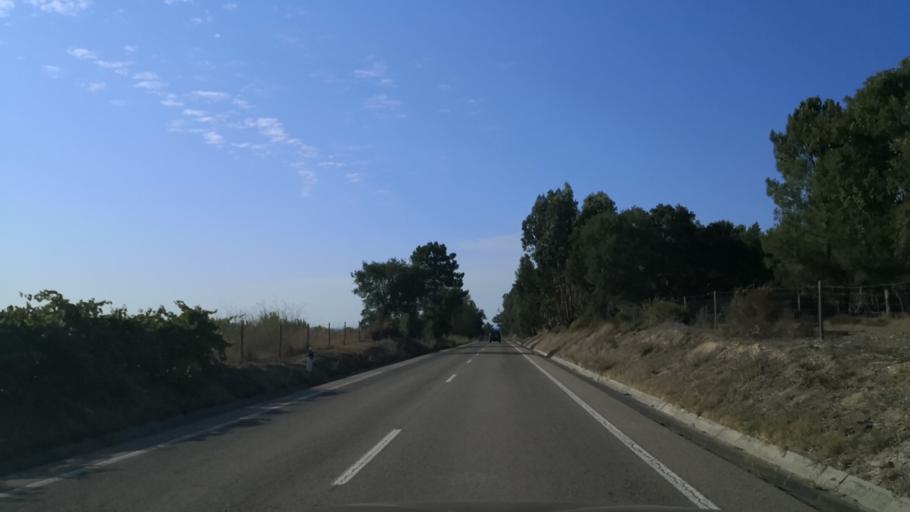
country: PT
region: Santarem
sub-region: Almeirim
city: Fazendas de Almeirim
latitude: 39.1397
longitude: -8.6121
